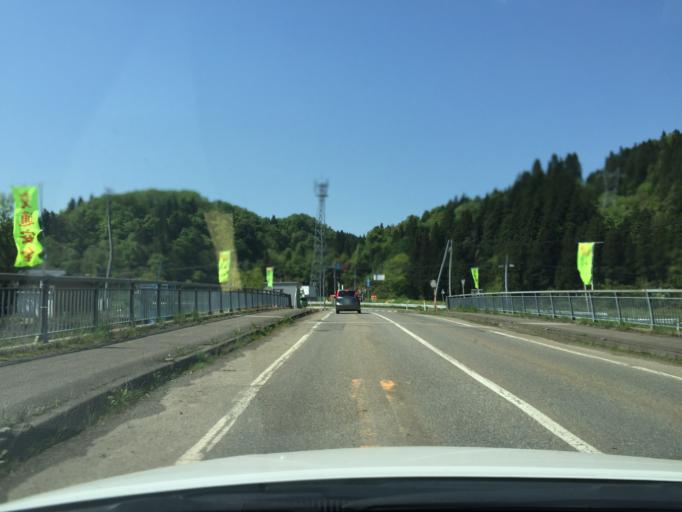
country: JP
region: Niigata
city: Kamo
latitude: 37.6319
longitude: 139.0952
